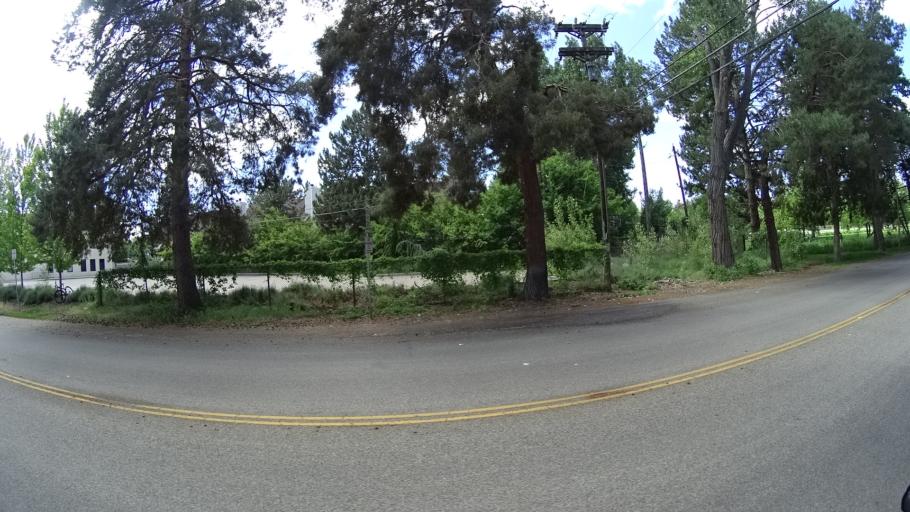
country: US
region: Idaho
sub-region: Ada County
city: Boise
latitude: 43.6064
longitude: -116.2134
